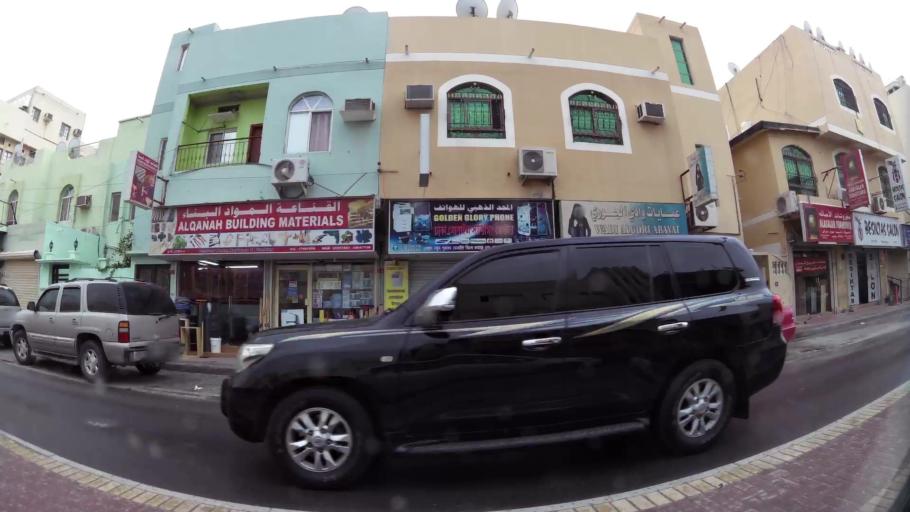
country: BH
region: Northern
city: Ar Rifa'
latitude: 26.1267
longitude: 50.5669
